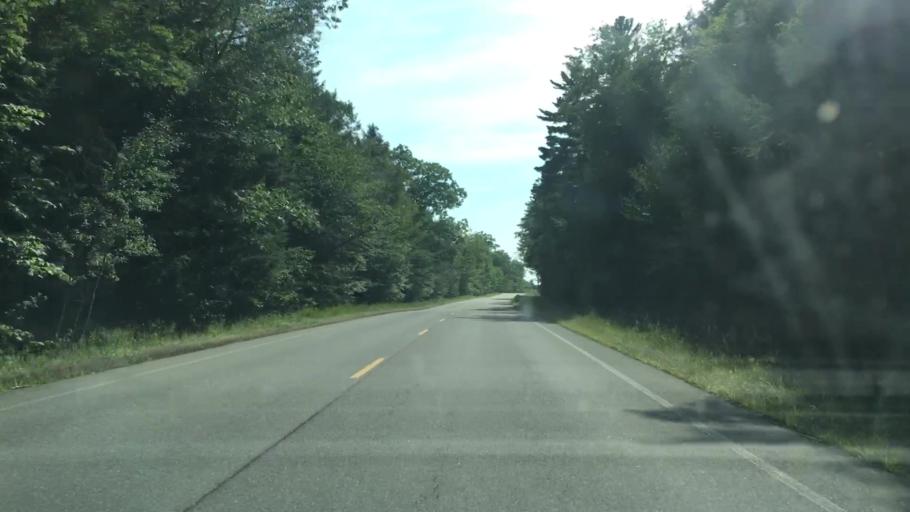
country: US
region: Maine
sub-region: Penobscot County
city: Lincoln
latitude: 45.3769
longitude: -68.5508
